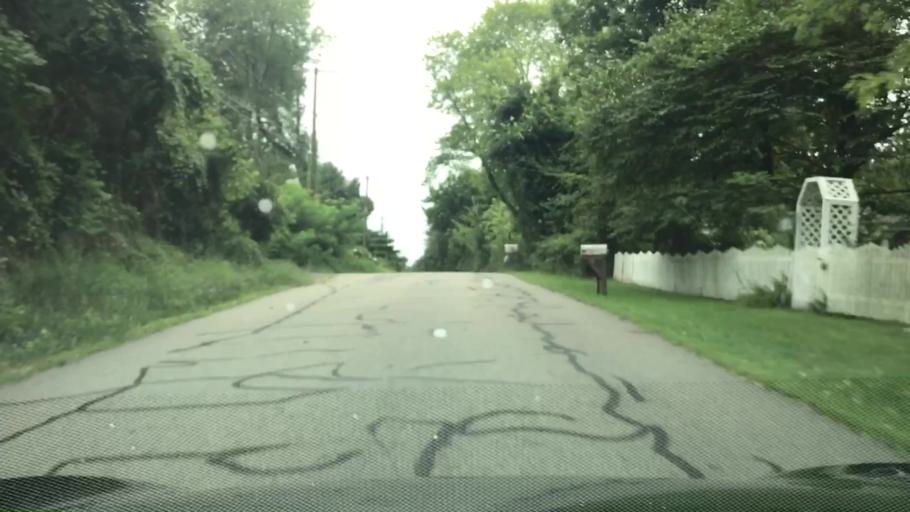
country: US
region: New Jersey
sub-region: Hunterdon County
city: Whitehouse Station
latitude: 40.6344
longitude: -74.7925
